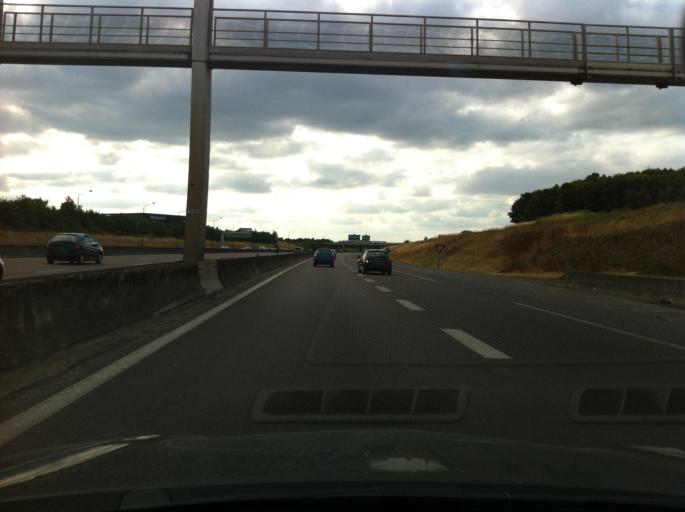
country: FR
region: Ile-de-France
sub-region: Departement de Seine-et-Marne
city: Lieusaint
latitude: 48.6209
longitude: 2.5482
